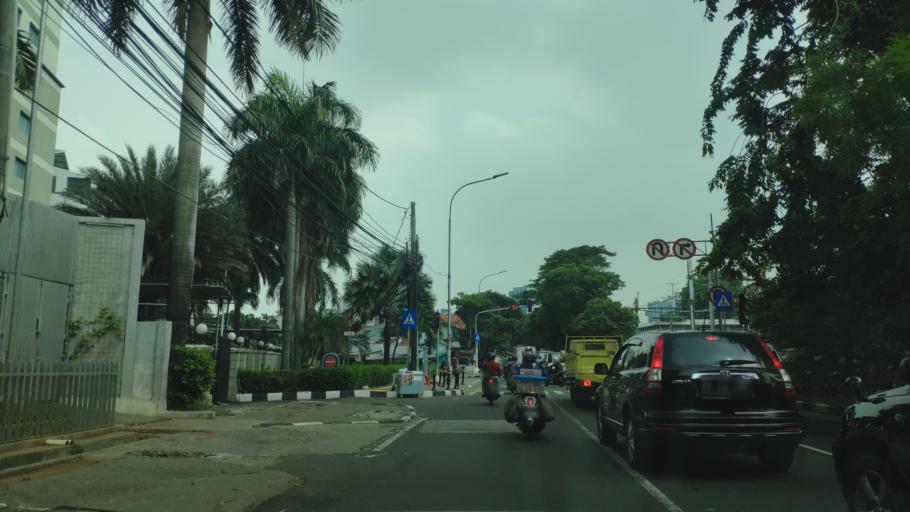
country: ID
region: Jakarta Raya
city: Jakarta
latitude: -6.2097
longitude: 106.7962
